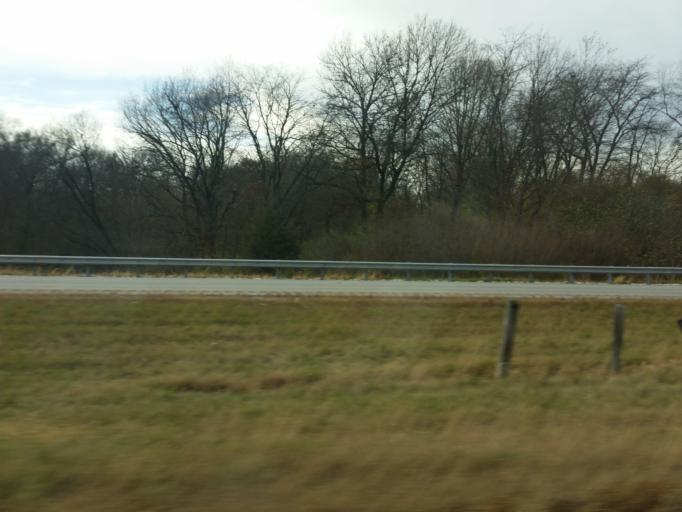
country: US
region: Illinois
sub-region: Henry County
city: Green Rock
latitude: 41.4472
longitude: -90.3678
